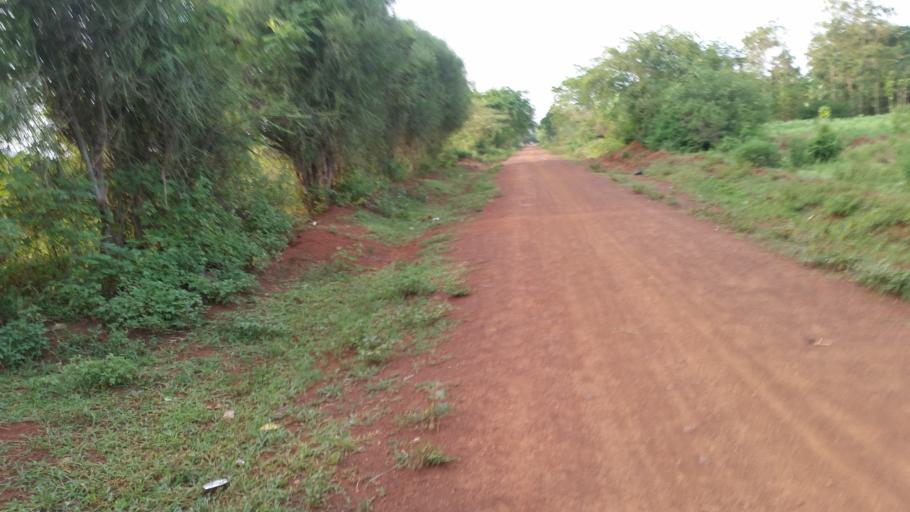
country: UG
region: Eastern Region
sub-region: Busia District
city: Busia
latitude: 0.5297
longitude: 34.0429
